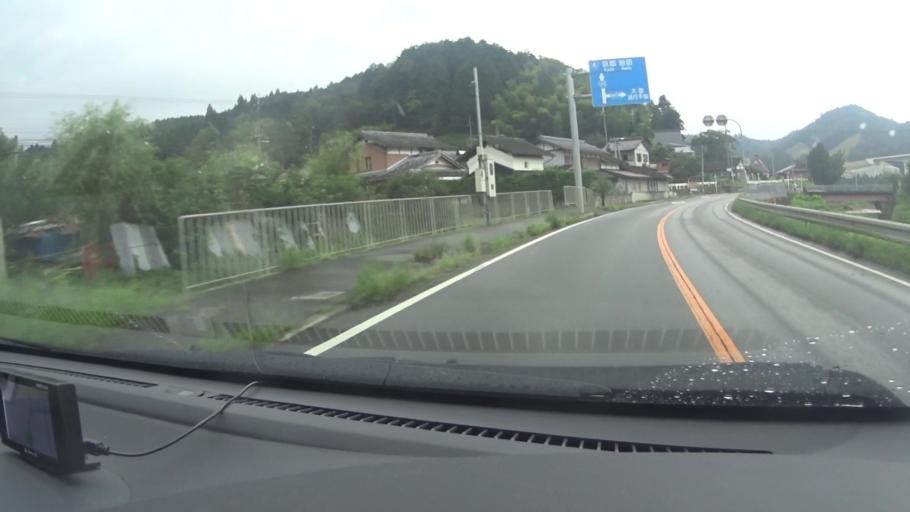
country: JP
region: Kyoto
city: Ayabe
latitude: 35.1948
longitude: 135.3620
